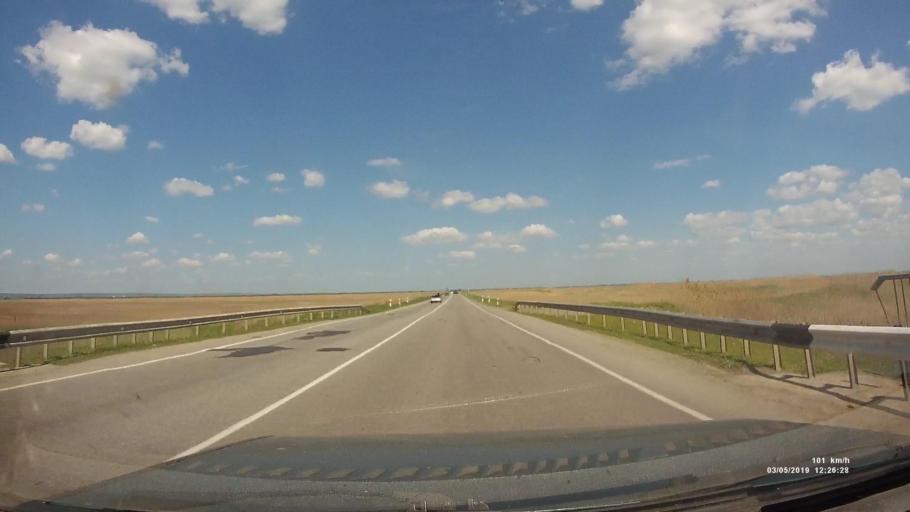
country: RU
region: Rostov
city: Semikarakorsk
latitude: 47.4458
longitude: 40.7140
